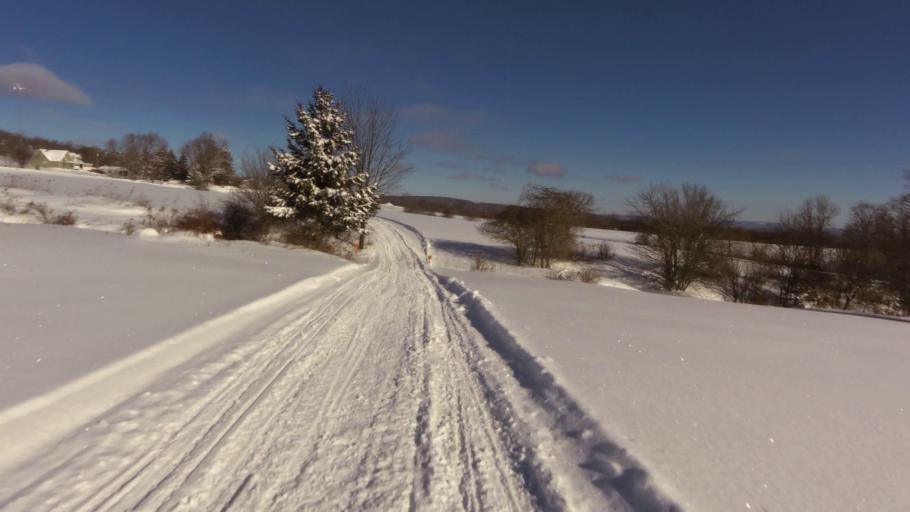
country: US
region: New York
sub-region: Chautauqua County
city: Falconer
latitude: 42.2706
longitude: -79.1137
